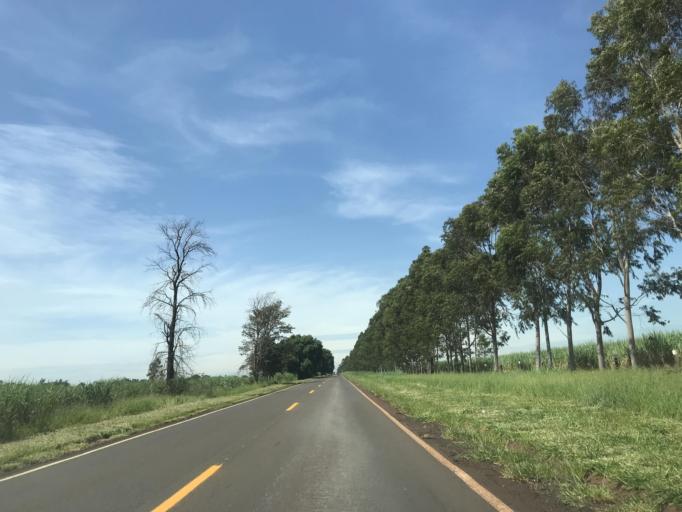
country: BR
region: Parana
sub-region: Paranavai
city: Nova Aurora
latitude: -22.8430
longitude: -52.6570
